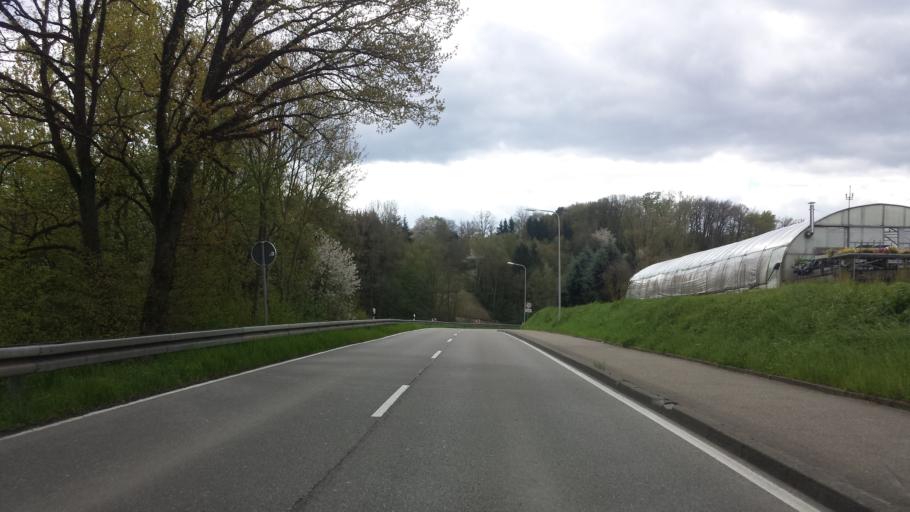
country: DE
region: Baden-Wuerttemberg
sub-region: Karlsruhe Region
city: Niefern-Oschelbronn
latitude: 48.9071
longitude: 8.7902
